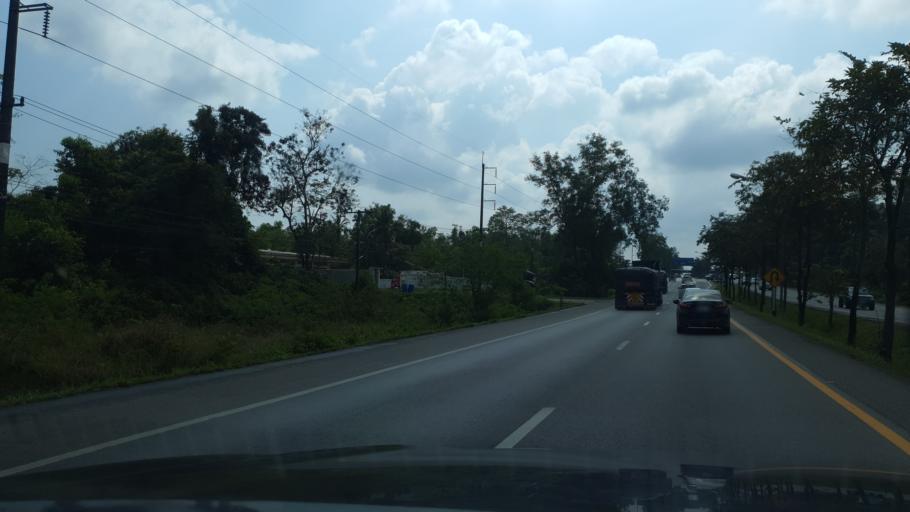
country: TH
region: Chumphon
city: Chumphon
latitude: 10.5535
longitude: 99.1171
